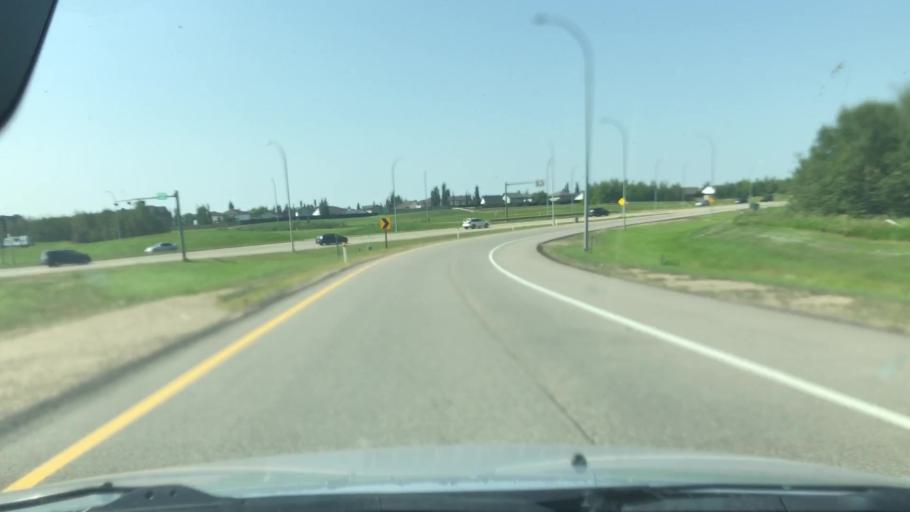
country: CA
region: Alberta
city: St. Albert
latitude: 53.5131
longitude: -113.6619
